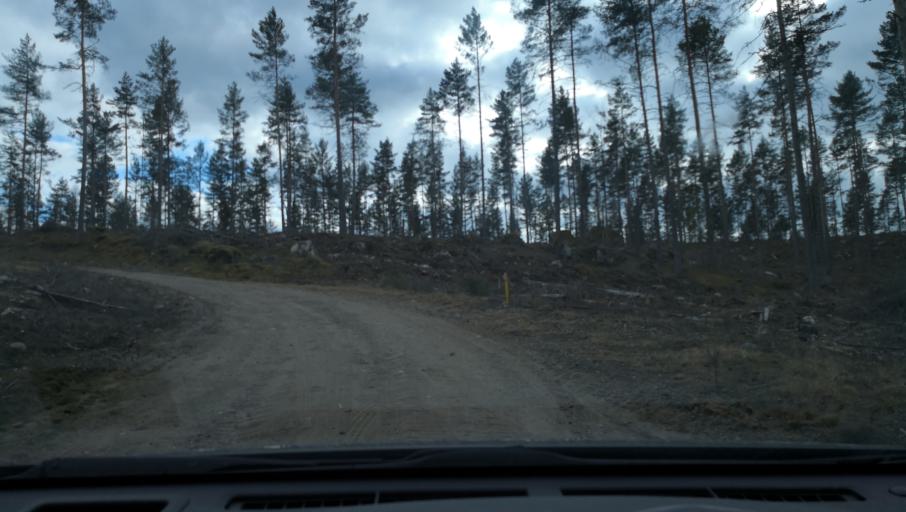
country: SE
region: Soedermanland
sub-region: Katrineholms Kommun
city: Katrineholm
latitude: 59.1308
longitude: 16.1550
